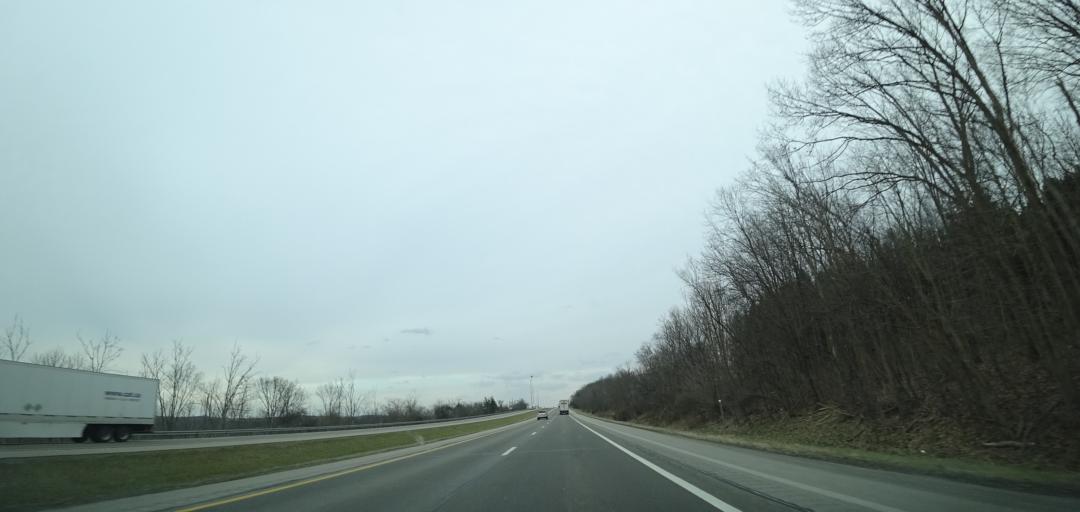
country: US
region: Ohio
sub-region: Mahoning County
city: New Middletown
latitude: 40.9313
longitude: -80.5695
